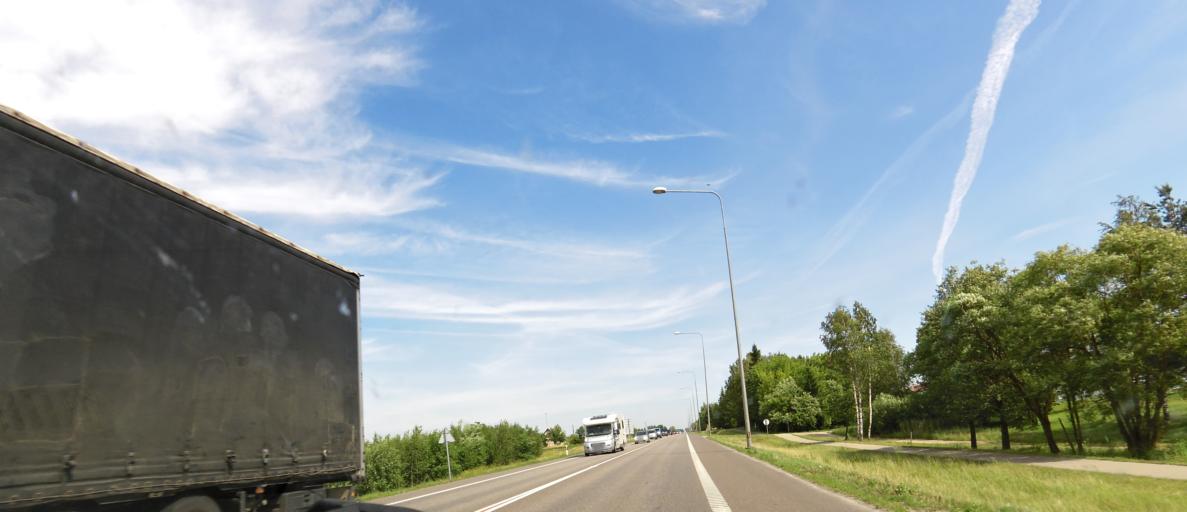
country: LT
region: Panevezys
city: Pasvalys
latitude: 55.9301
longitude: 24.3358
